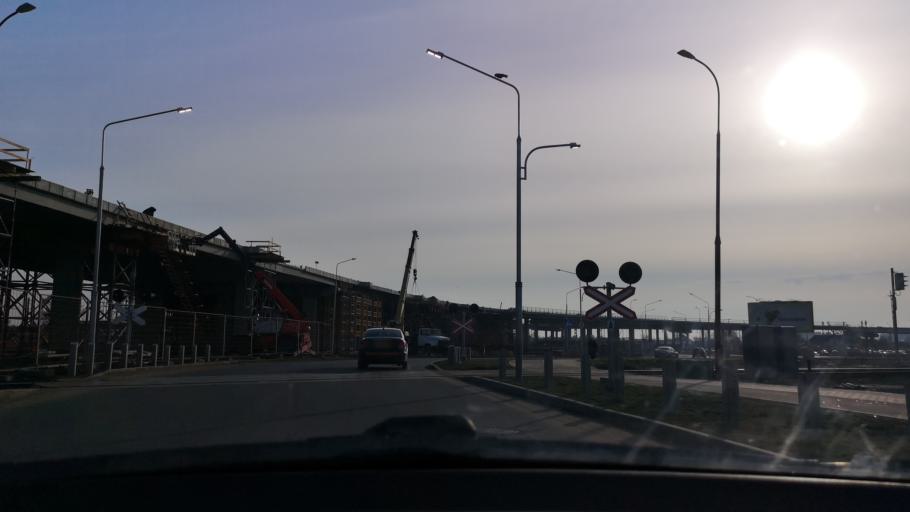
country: BY
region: Brest
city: Brest
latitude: 52.1073
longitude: 23.6658
